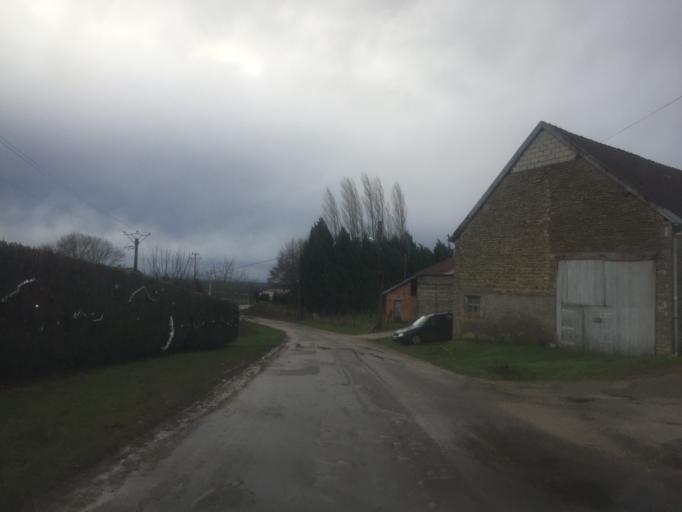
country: FR
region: Franche-Comte
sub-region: Departement du Jura
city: Dampierre
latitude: 47.2070
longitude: 5.7096
